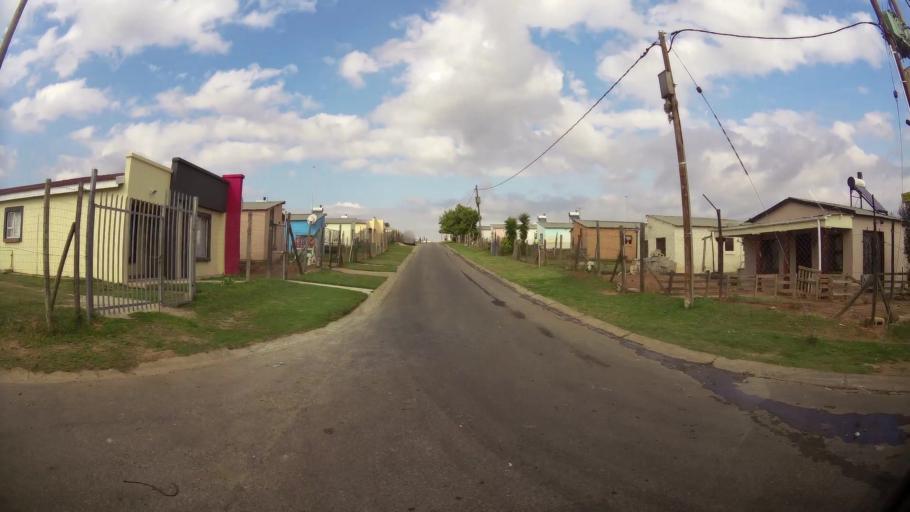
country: ZA
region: Eastern Cape
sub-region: Nelson Mandela Bay Metropolitan Municipality
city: Uitenhage
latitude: -33.7475
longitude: 25.3932
